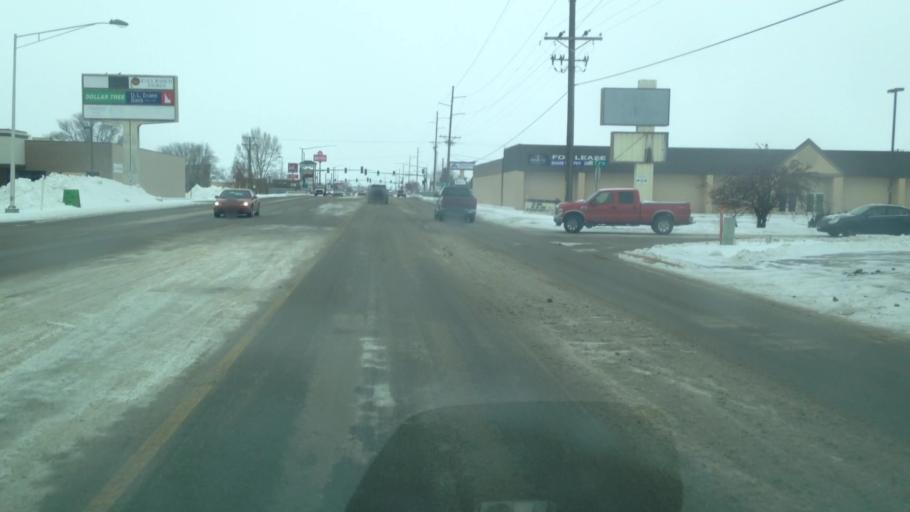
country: US
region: Idaho
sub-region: Madison County
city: Rexburg
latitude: 43.8337
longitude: -111.7781
